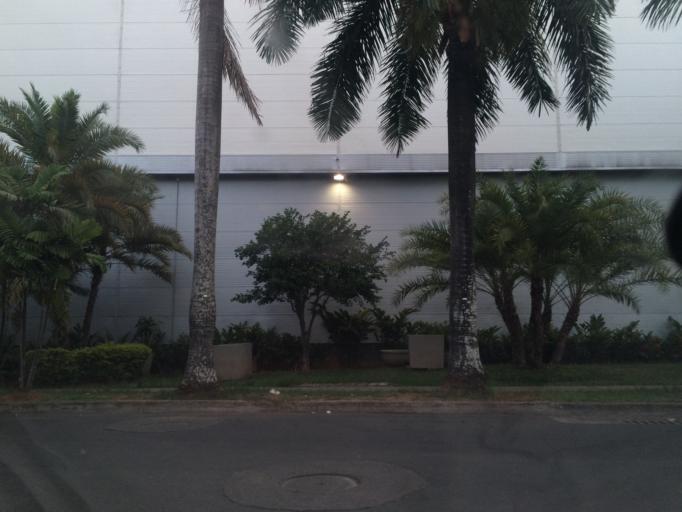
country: CO
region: Valle del Cauca
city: Cali
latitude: 3.4136
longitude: -76.5401
